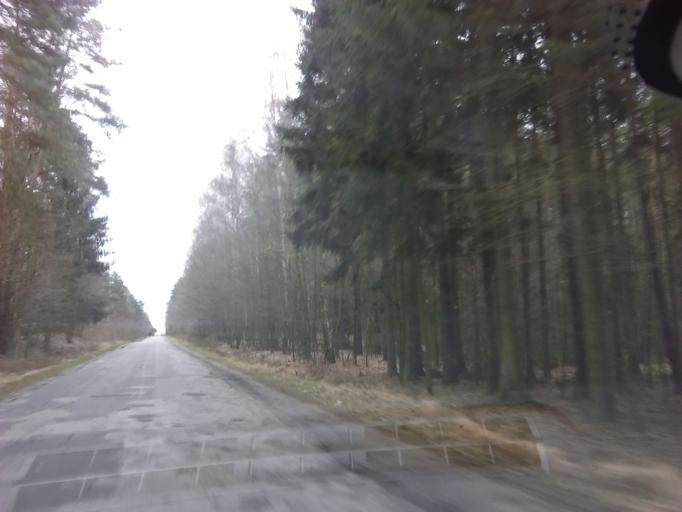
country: PL
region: Kujawsko-Pomorskie
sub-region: Powiat sepolenski
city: Sypniewo
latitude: 53.4505
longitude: 17.3863
